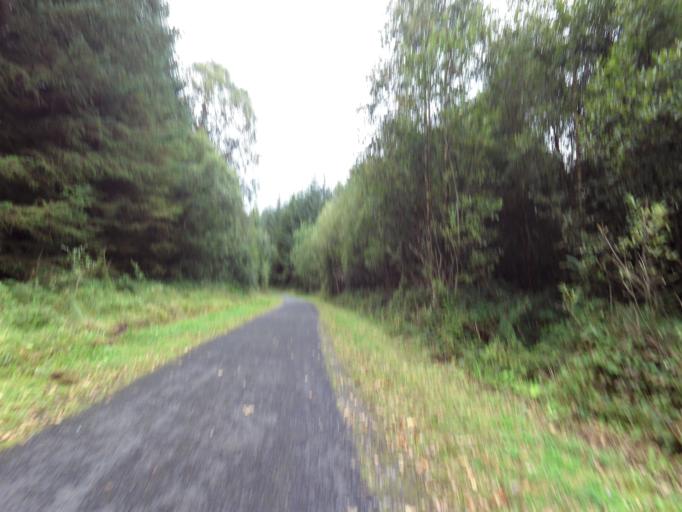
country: IE
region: Leinster
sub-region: Uibh Fhaili
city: Ferbane
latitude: 53.2154
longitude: -7.7388
